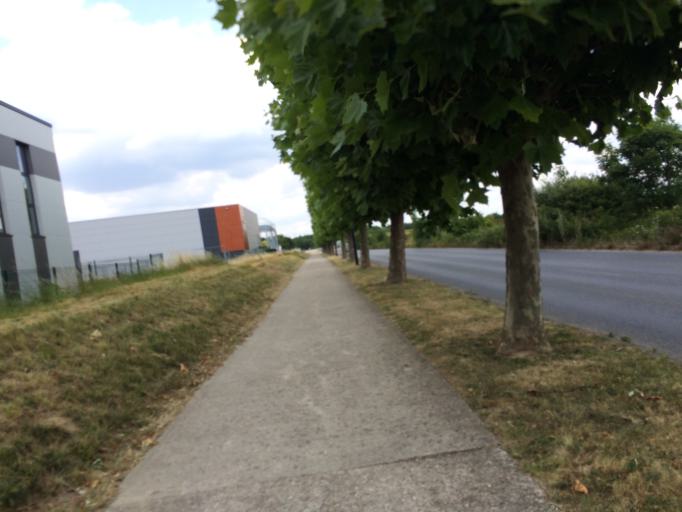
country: FR
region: Ile-de-France
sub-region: Departement de l'Essonne
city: Tigery
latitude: 48.6265
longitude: 2.5188
